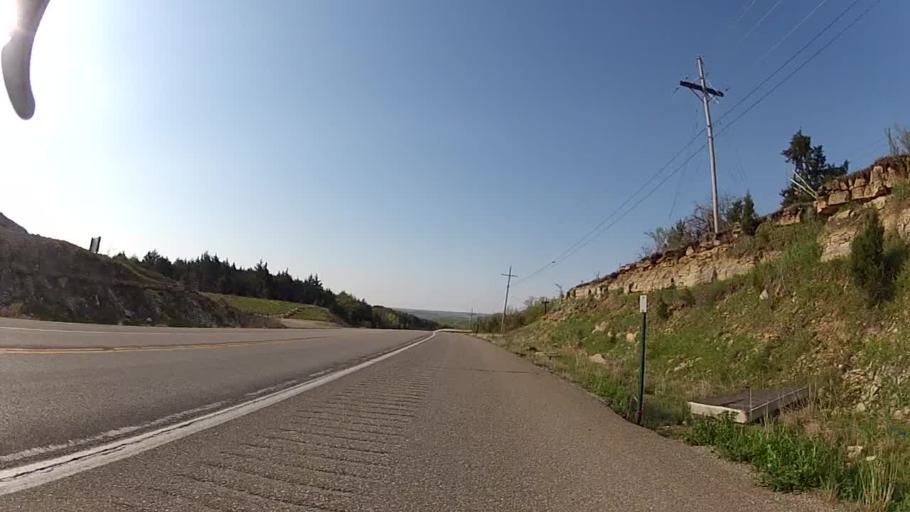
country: US
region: Kansas
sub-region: Riley County
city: Manhattan
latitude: 39.1749
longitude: -96.6470
